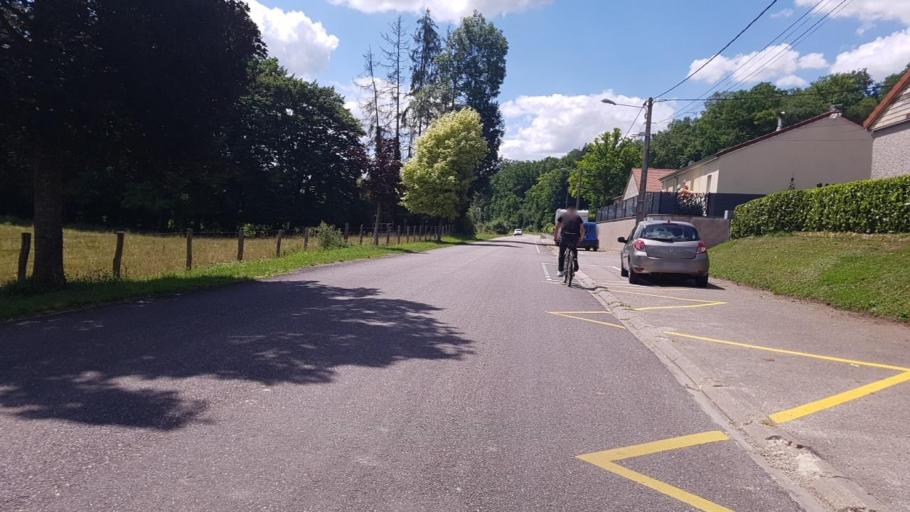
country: FR
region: Lorraine
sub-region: Departement de la Meuse
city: Vacon
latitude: 48.6782
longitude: 5.6102
